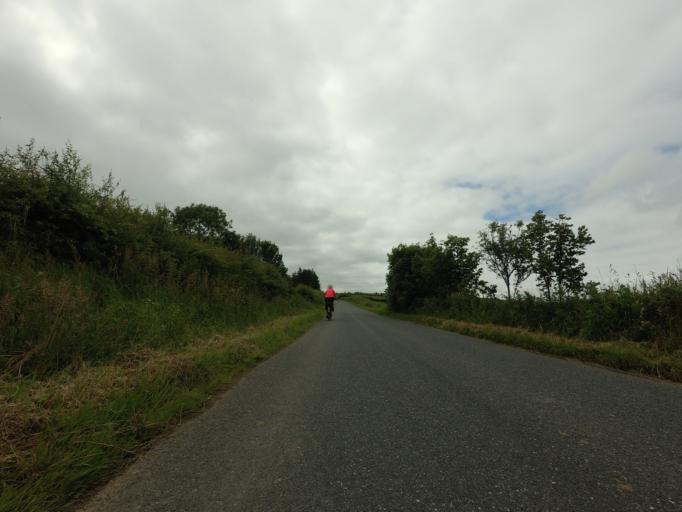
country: GB
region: Scotland
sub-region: Aberdeenshire
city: Rosehearty
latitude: 57.5434
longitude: -2.2360
